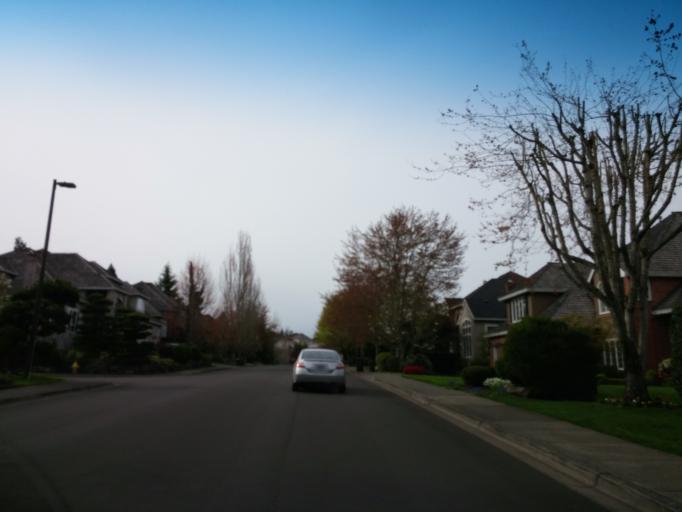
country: US
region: Oregon
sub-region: Washington County
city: Cedar Mill
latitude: 45.5407
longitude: -122.8086
